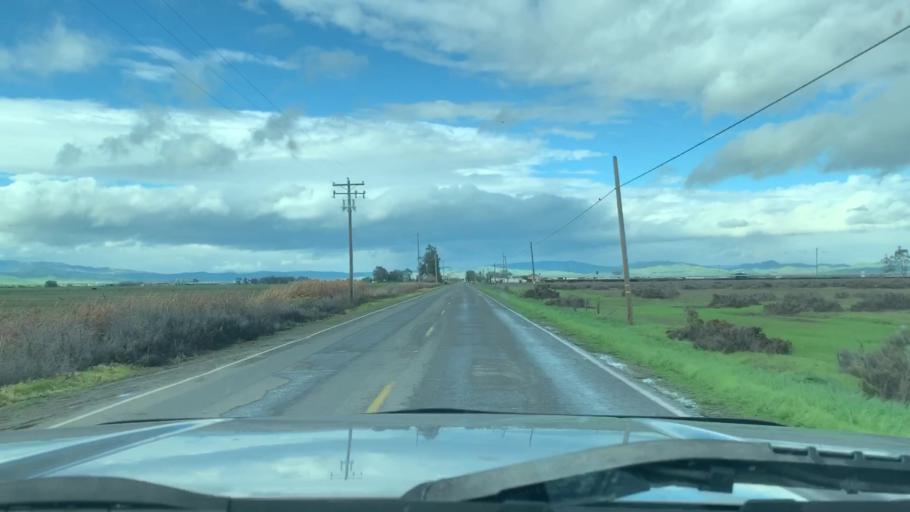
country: US
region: California
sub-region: Merced County
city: Los Banos
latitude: 37.1000
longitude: -120.8938
